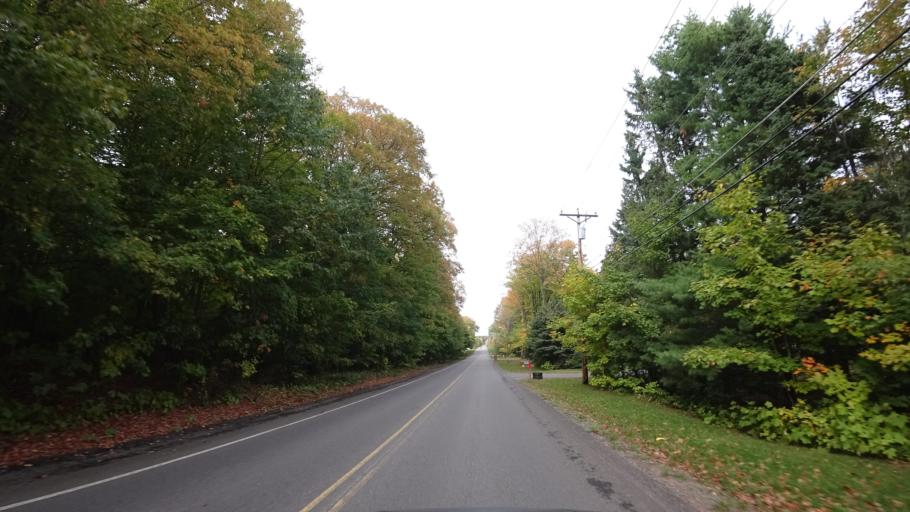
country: US
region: Michigan
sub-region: Marquette County
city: Trowbridge Park
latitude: 46.5368
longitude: -87.4374
